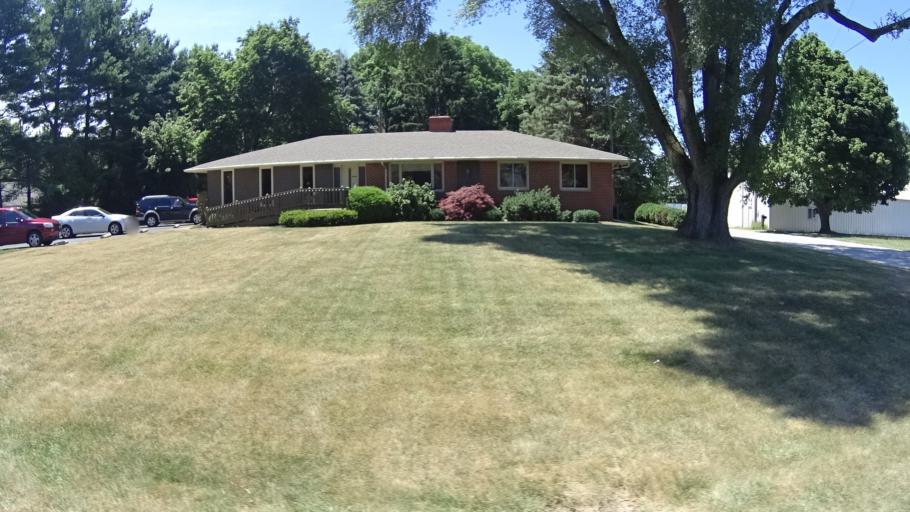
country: US
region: Ohio
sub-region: Erie County
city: Sandusky
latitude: 41.4223
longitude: -82.7033
